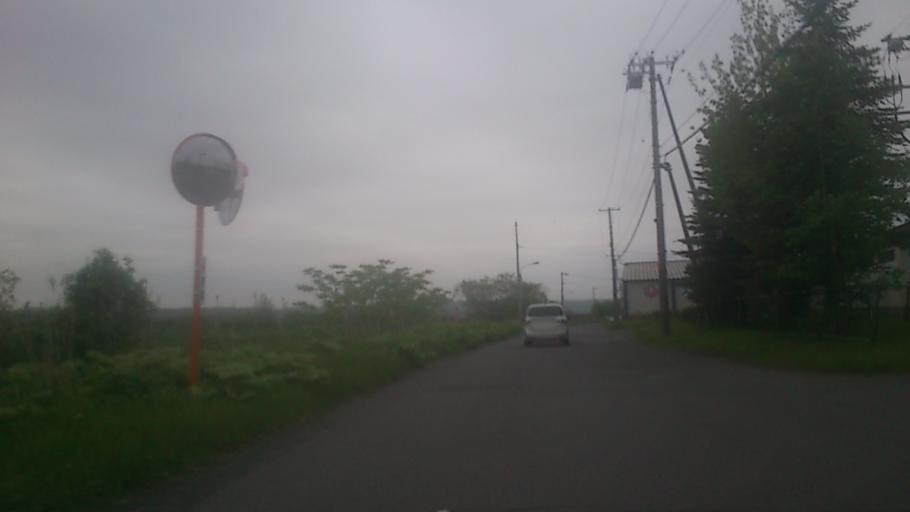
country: JP
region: Hokkaido
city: Kushiro
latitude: 42.9993
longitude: 144.4162
